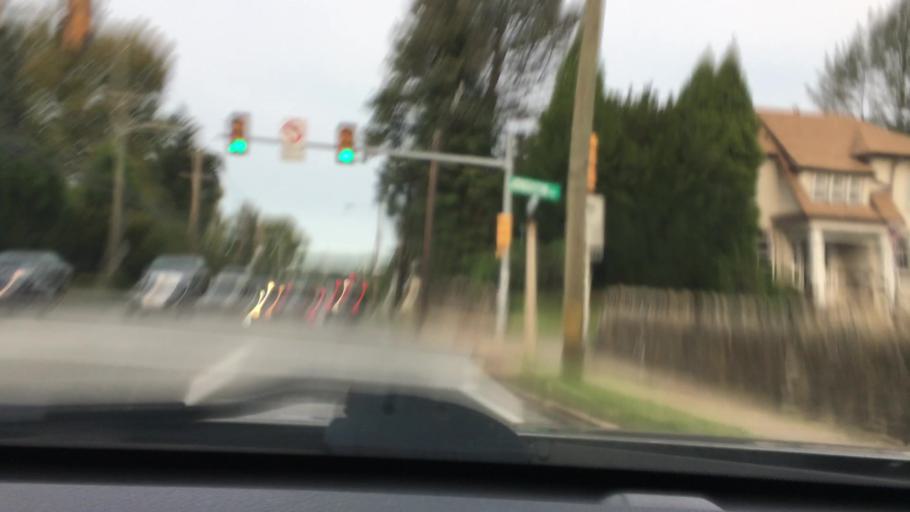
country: US
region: Pennsylvania
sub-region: Delaware County
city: Drexel Hill
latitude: 39.9697
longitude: -75.2918
